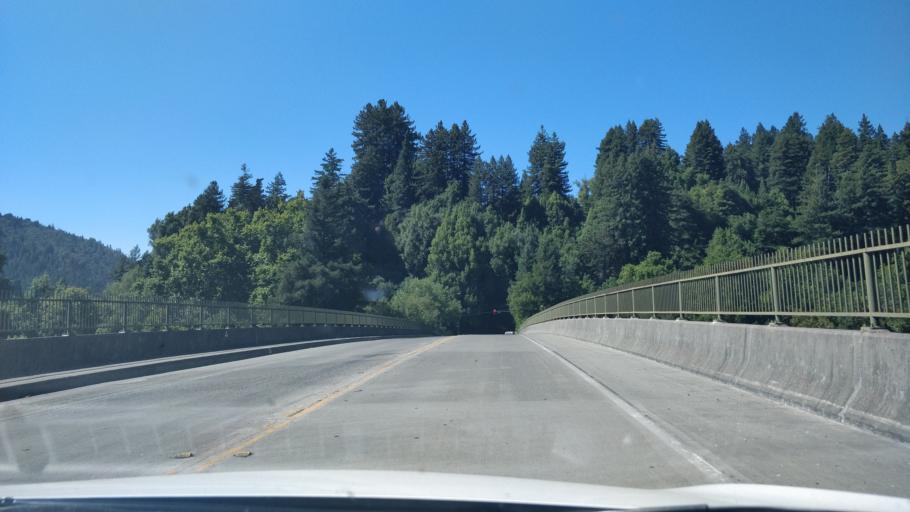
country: US
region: California
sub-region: Sonoma County
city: Guerneville
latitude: 38.5011
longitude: -122.9945
